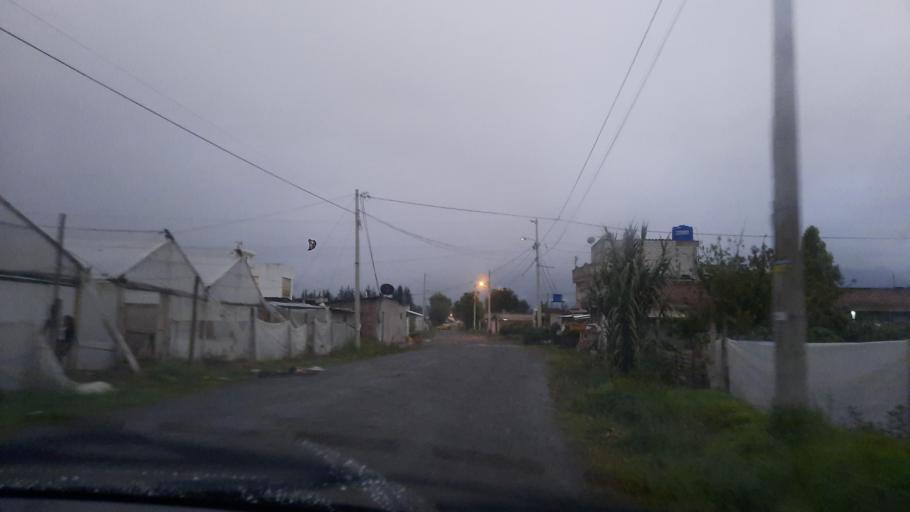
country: EC
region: Chimborazo
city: Riobamba
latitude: -1.6883
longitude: -78.6666
